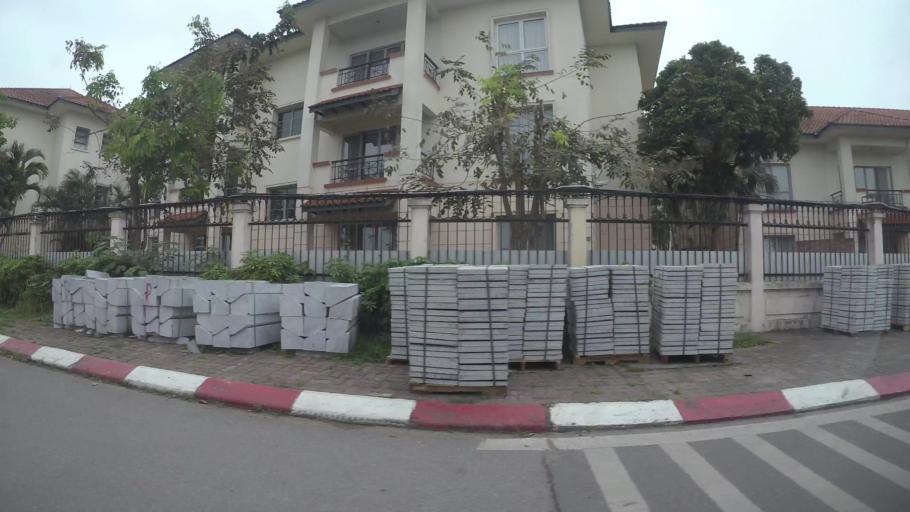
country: VN
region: Ha Noi
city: Tay Ho
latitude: 21.0672
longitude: 105.8192
